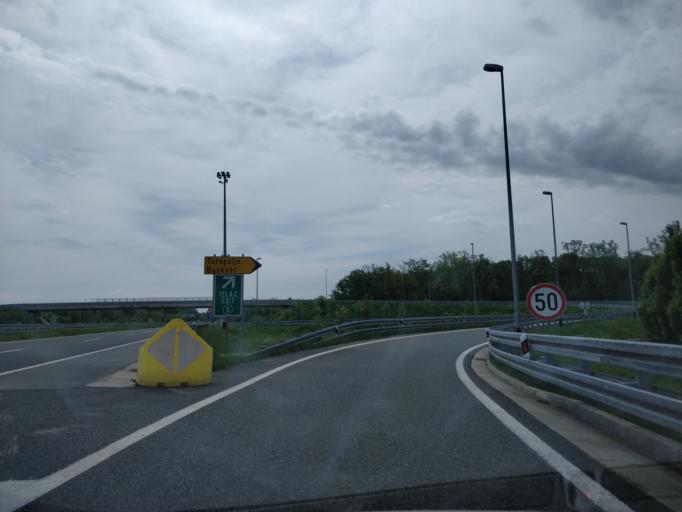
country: HR
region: Zagrebacka
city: Mraclin
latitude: 45.6208
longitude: 16.1021
